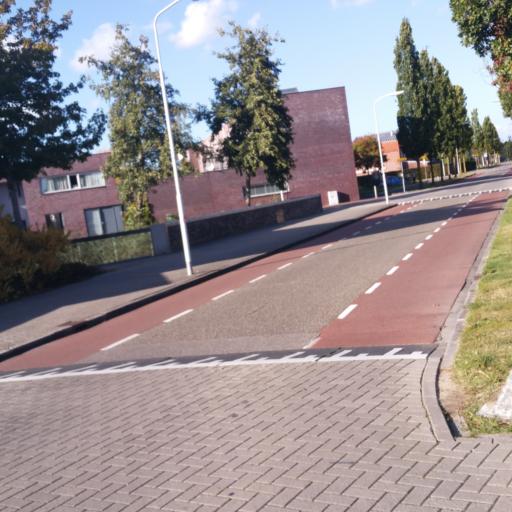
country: NL
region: Utrecht
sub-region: Gemeente IJsselstein
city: IJsselstein
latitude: 52.0091
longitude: 5.0365
